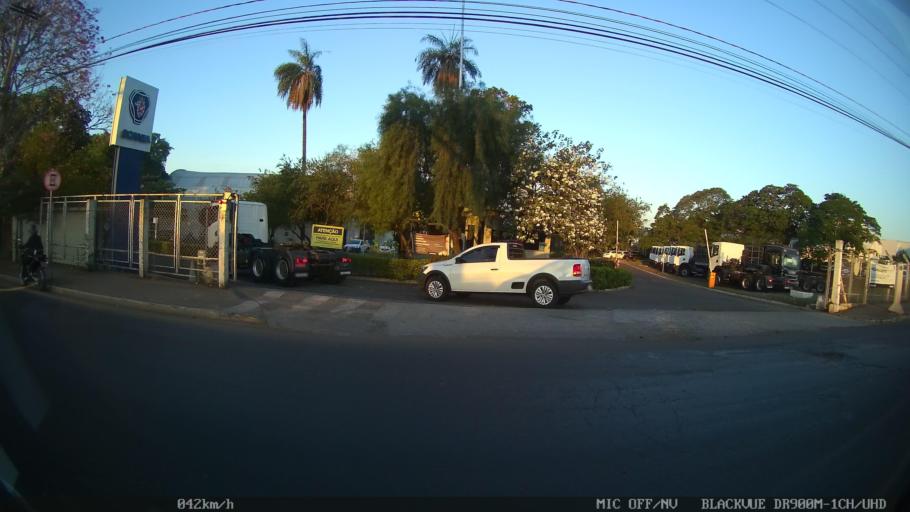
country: BR
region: Sao Paulo
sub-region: Sao Jose Do Rio Preto
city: Sao Jose do Rio Preto
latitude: -20.7867
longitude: -49.3533
